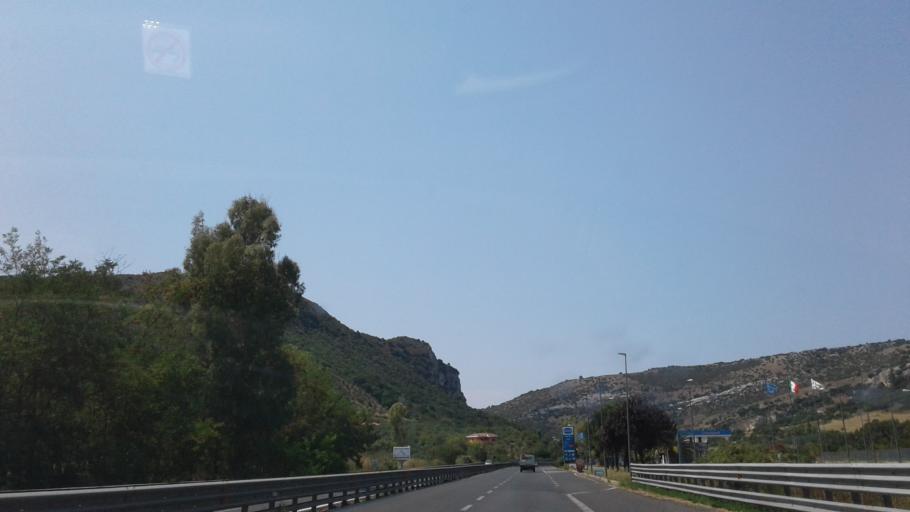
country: IT
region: Sardinia
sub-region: Provincia di Sassari
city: Muros
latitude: 40.6918
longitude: 8.6220
